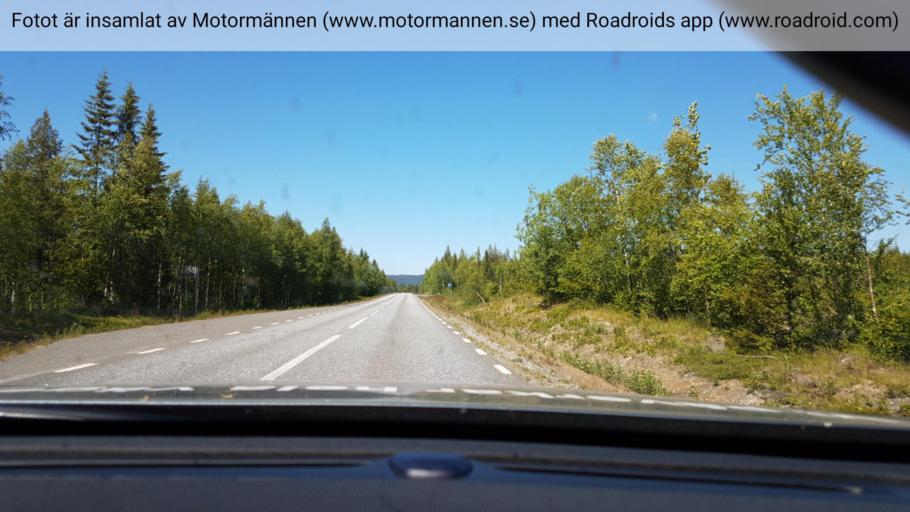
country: SE
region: Vaesterbotten
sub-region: Vilhelmina Kommun
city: Sjoberg
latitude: 64.8546
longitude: 15.9024
